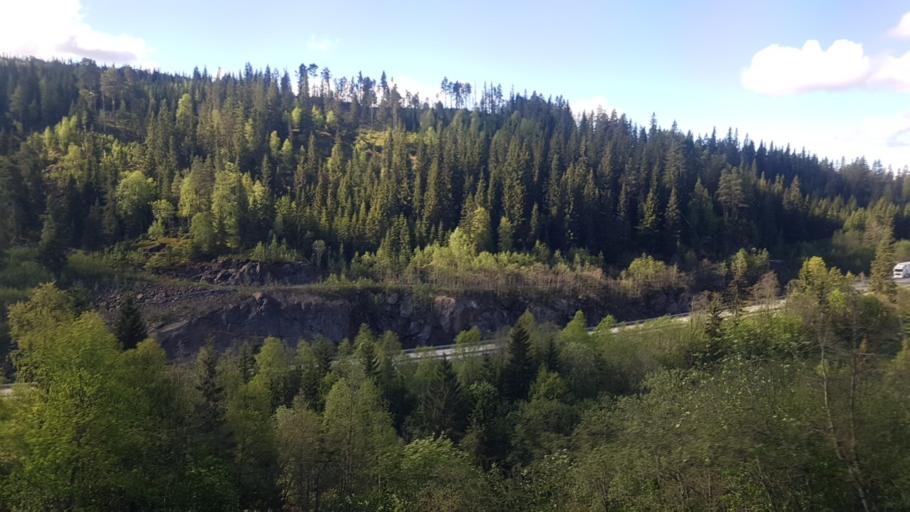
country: NO
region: Sor-Trondelag
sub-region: Midtre Gauldal
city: Storen
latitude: 62.9962
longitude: 10.2412
